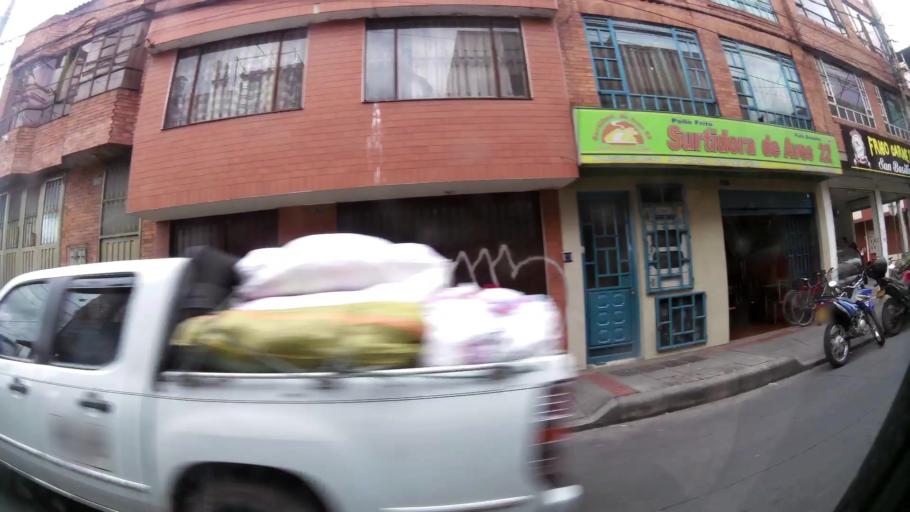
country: CO
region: Cundinamarca
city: Funza
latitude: 4.7025
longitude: -74.1232
